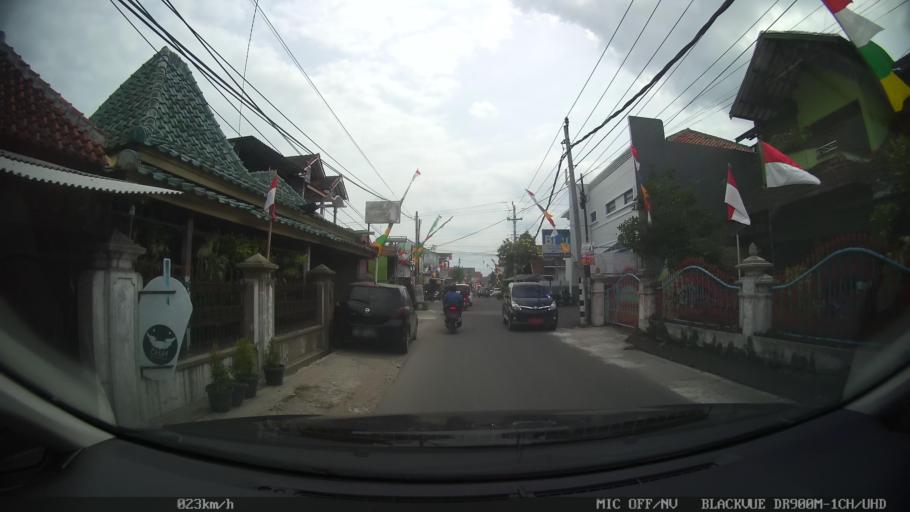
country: ID
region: Daerah Istimewa Yogyakarta
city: Yogyakarta
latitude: -7.7963
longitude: 110.4015
